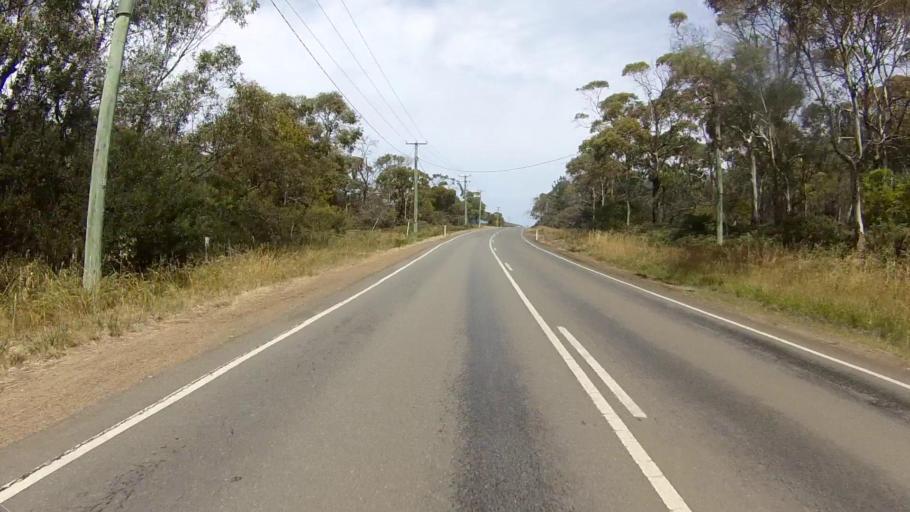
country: AU
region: Tasmania
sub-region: Clarence
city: Sandford
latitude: -43.0194
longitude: 147.4885
